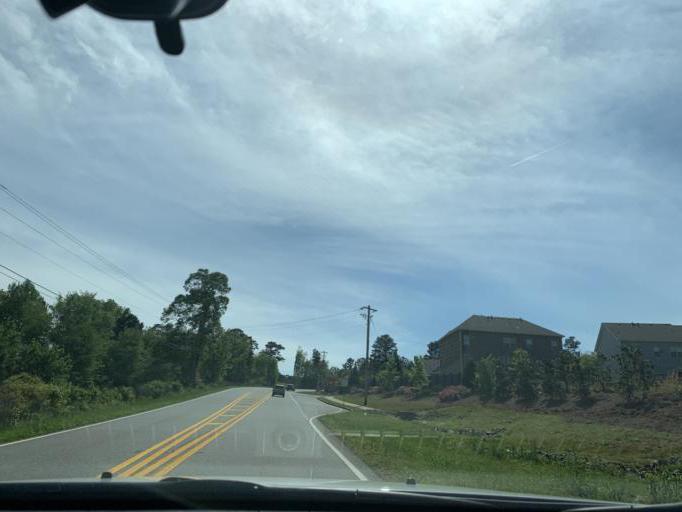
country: US
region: Georgia
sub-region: Forsyth County
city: Cumming
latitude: 34.2829
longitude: -84.1710
